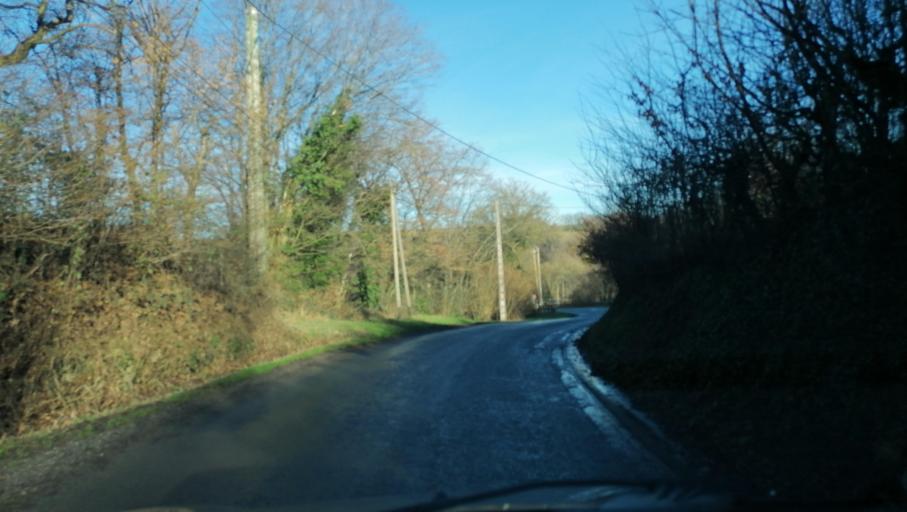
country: FR
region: Nord-Pas-de-Calais
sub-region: Departement du Nord
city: Recquignies
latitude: 50.2036
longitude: 4.0646
